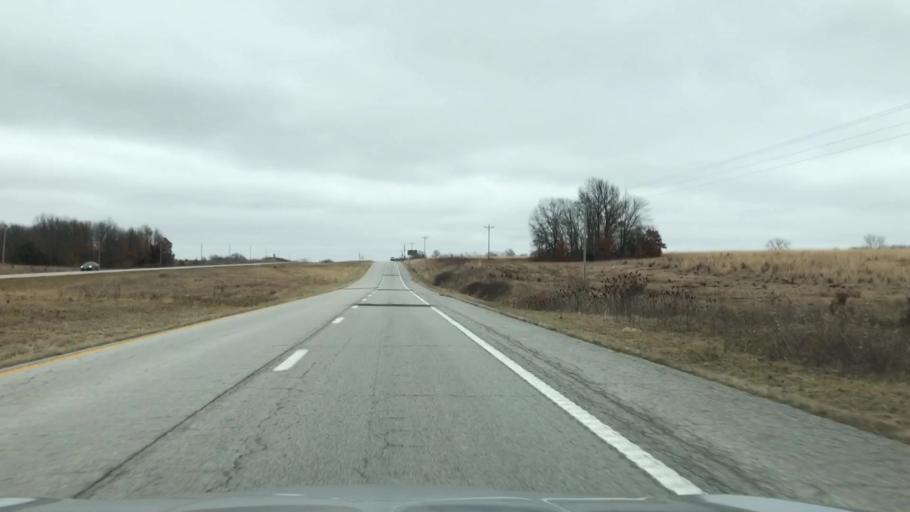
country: US
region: Missouri
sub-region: Linn County
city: Linneus
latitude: 39.7782
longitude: -93.1869
